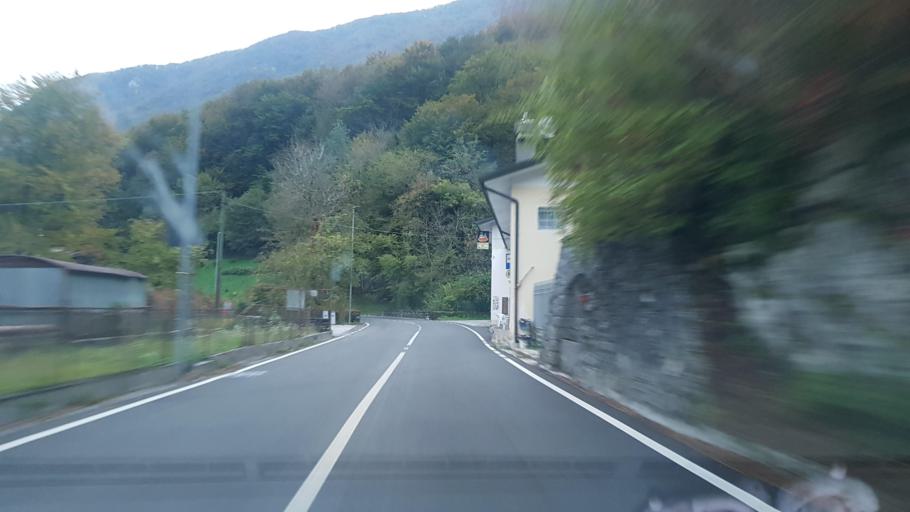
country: IT
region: Friuli Venezia Giulia
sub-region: Provincia di Pordenone
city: Anduins
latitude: 46.2632
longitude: 12.9533
